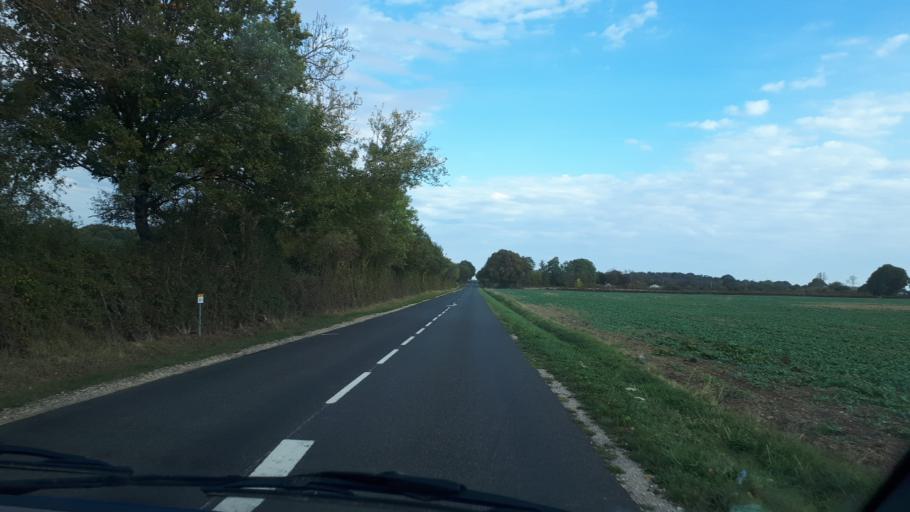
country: FR
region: Centre
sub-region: Departement du Loir-et-Cher
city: Mondoubleau
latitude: 47.9363
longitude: 0.9335
